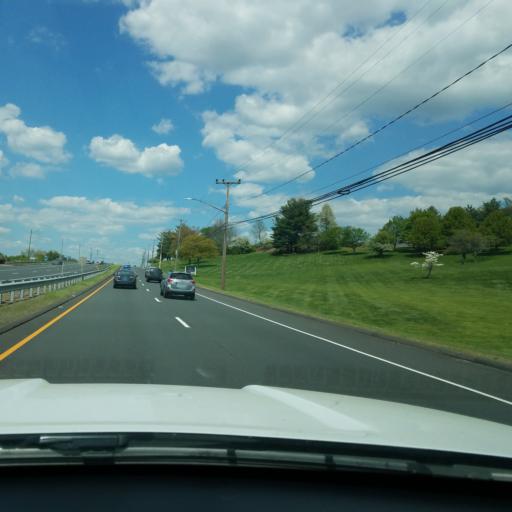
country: US
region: Connecticut
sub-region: Hartford County
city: Kensington
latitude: 41.6494
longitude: -72.7287
